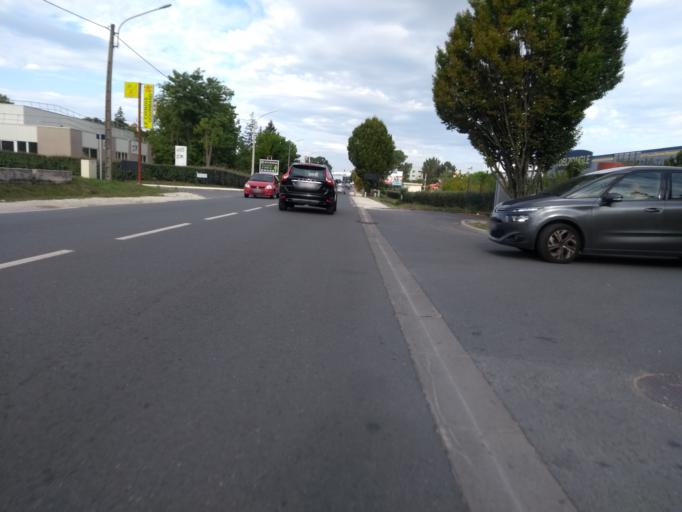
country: FR
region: Aquitaine
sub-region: Departement de la Gironde
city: Canejan
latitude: 44.7864
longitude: -0.6442
